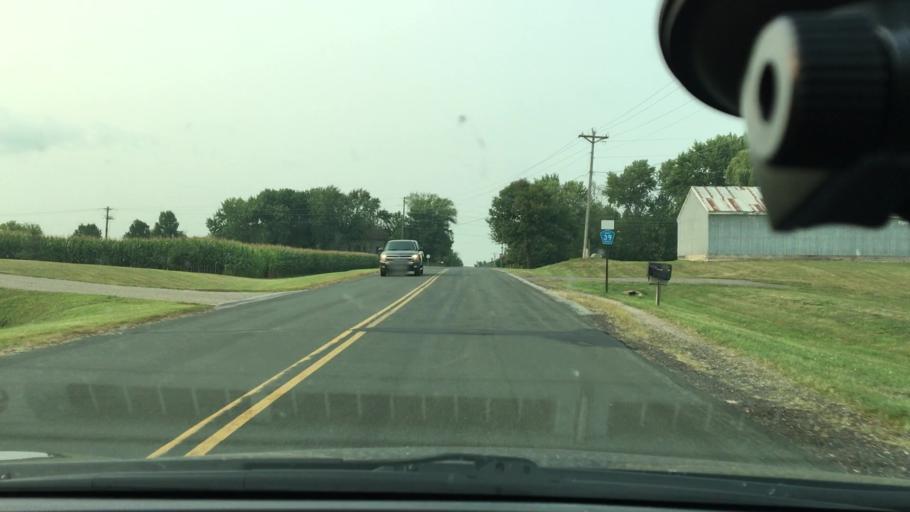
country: US
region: Minnesota
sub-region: Wright County
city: Albertville
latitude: 45.2888
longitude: -93.6839
